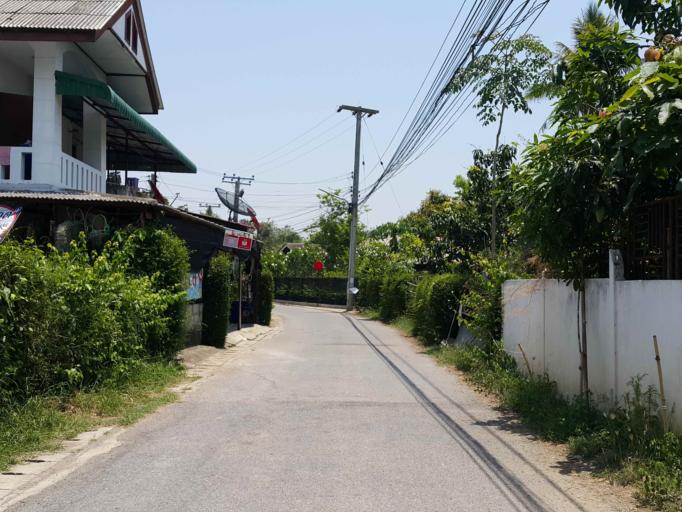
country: TH
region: Chiang Mai
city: San Kamphaeng
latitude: 18.8176
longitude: 99.1151
